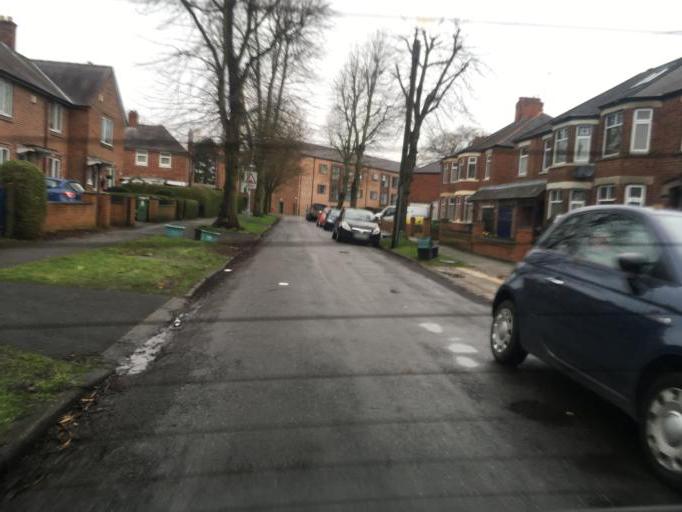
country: GB
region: England
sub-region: City of York
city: York
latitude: 53.9639
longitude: -1.0624
